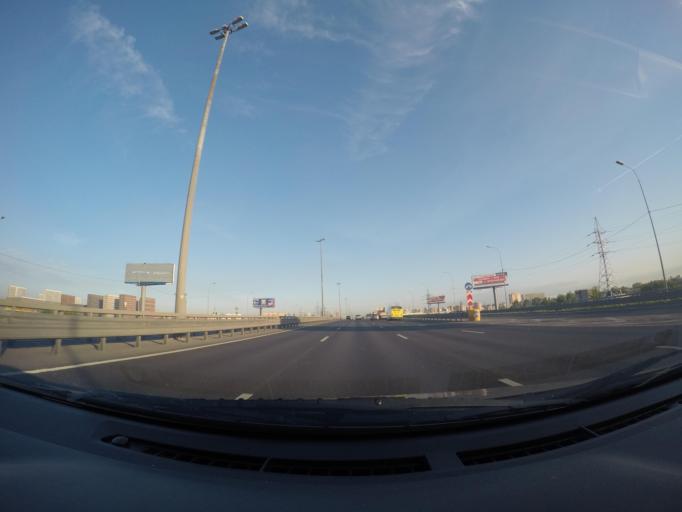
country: RU
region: Moskovskaya
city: Lyubertsy
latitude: 55.6601
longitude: 37.8910
